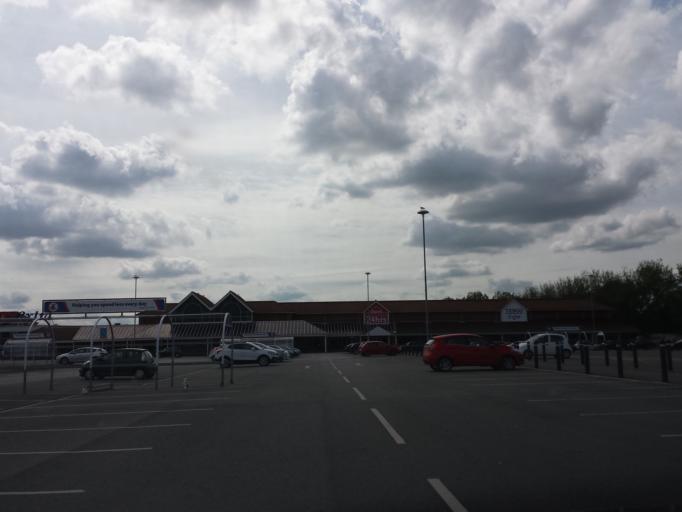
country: GB
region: England
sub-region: Hartlepool
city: Hartlepool
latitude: 54.6783
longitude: -1.2103
